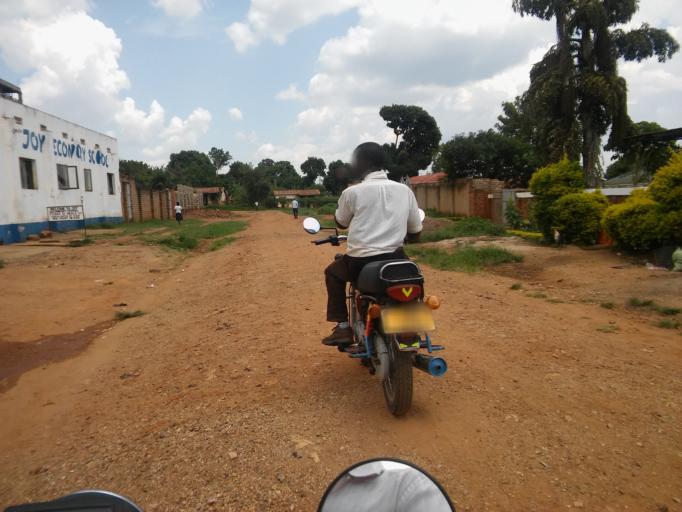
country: UG
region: Eastern Region
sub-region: Mbale District
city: Mbale
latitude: 1.0720
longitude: 34.1705
